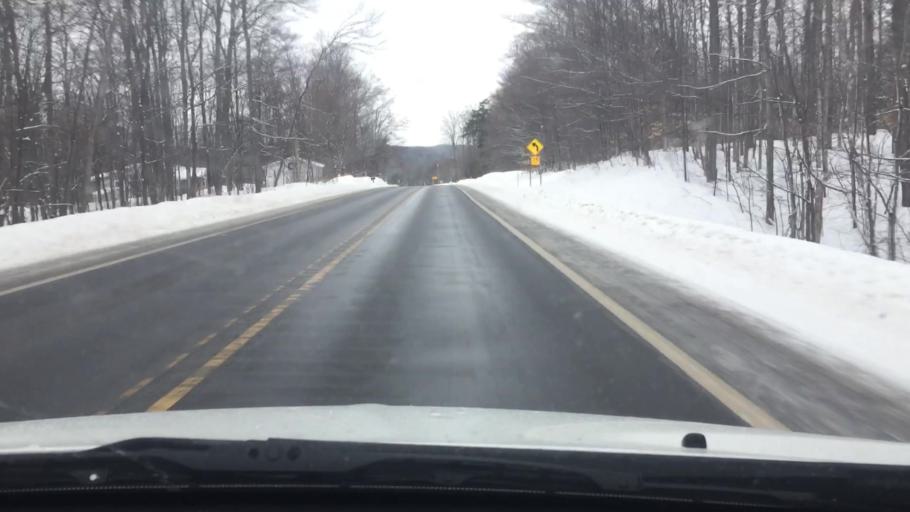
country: US
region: Michigan
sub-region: Charlevoix County
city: East Jordan
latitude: 45.1015
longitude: -85.0292
